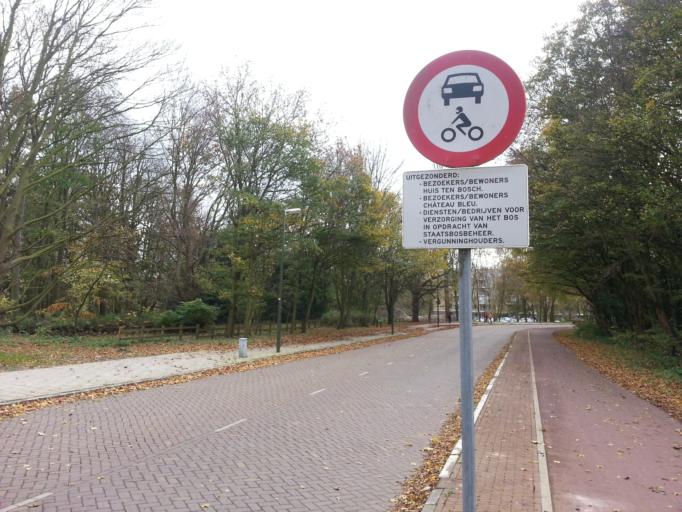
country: NL
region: South Holland
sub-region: Gemeente Leidschendam-Voorburg
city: Voorburg
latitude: 52.0983
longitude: 4.3466
